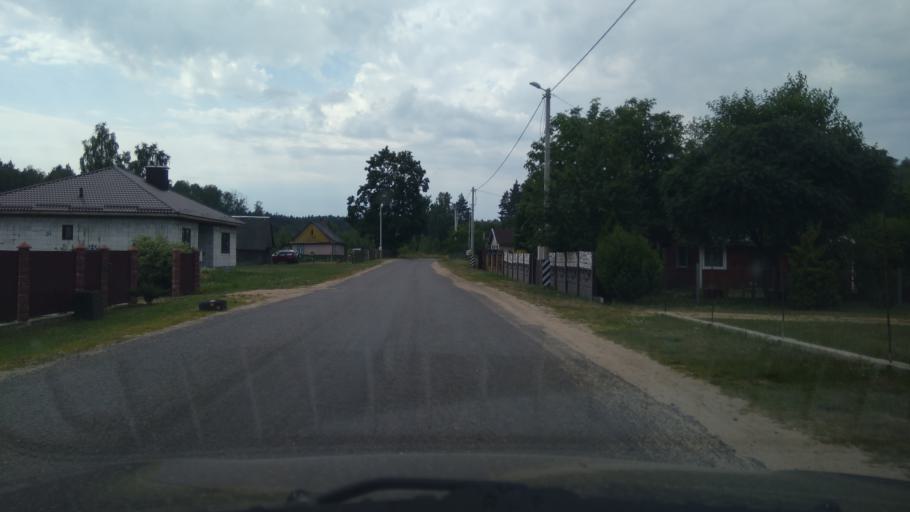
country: BY
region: Brest
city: Nyakhachava
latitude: 52.6089
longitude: 25.0862
